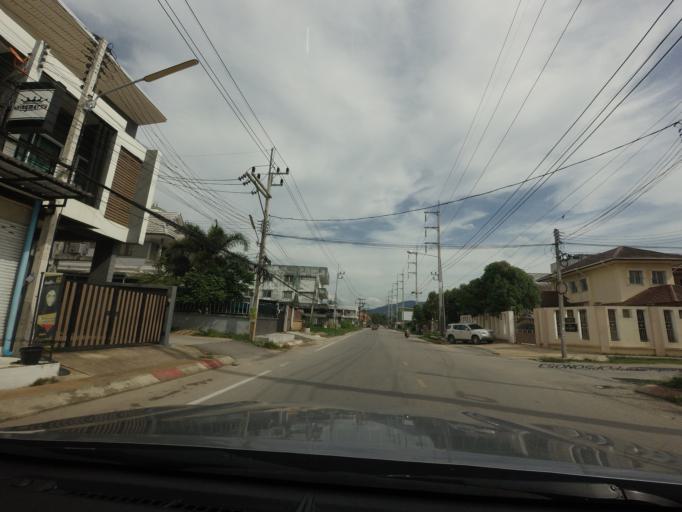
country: TH
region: Yala
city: Yala
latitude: 6.5339
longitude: 101.2928
